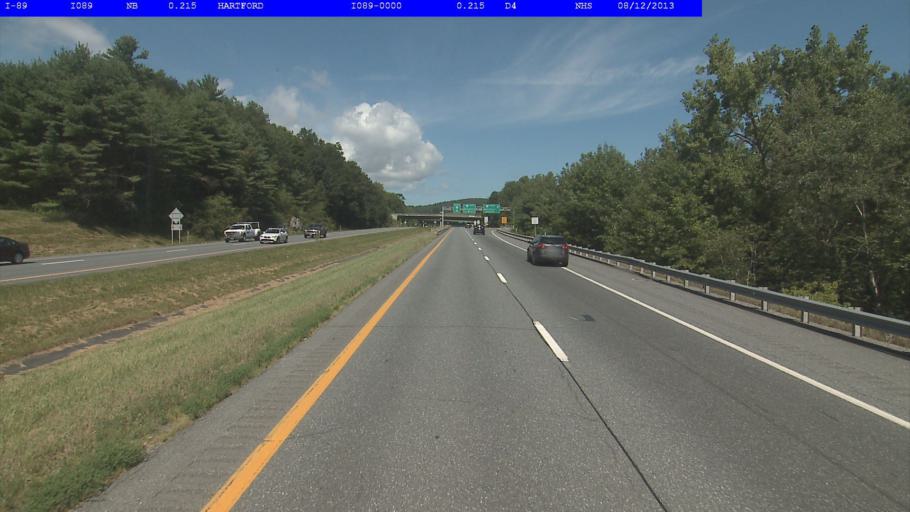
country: US
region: Vermont
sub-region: Windsor County
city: White River Junction
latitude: 43.6366
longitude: -72.3330
